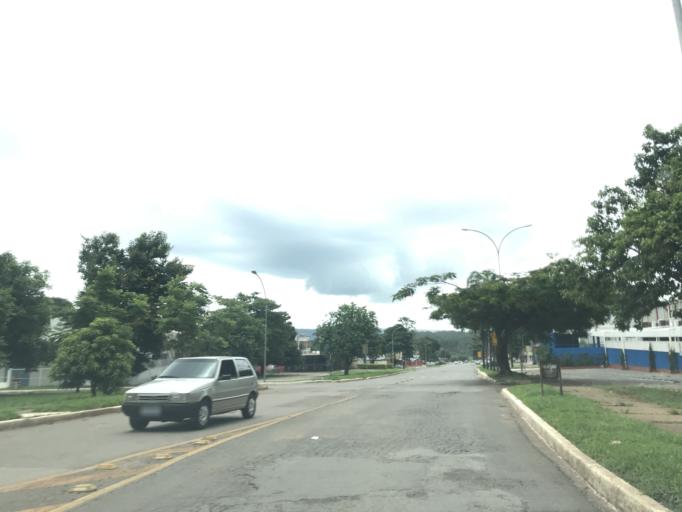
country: BR
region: Federal District
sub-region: Brasilia
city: Brasilia
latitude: -15.6431
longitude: -47.8026
